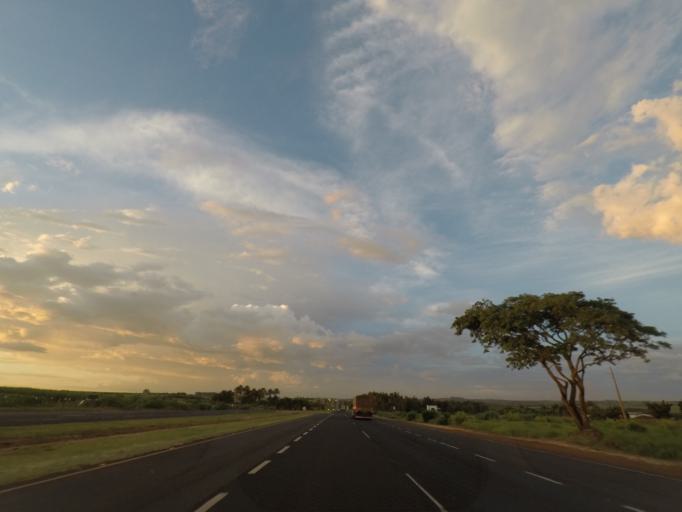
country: BR
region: Minas Gerais
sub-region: Uberaba
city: Uberaba
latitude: -19.6626
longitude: -48.0013
